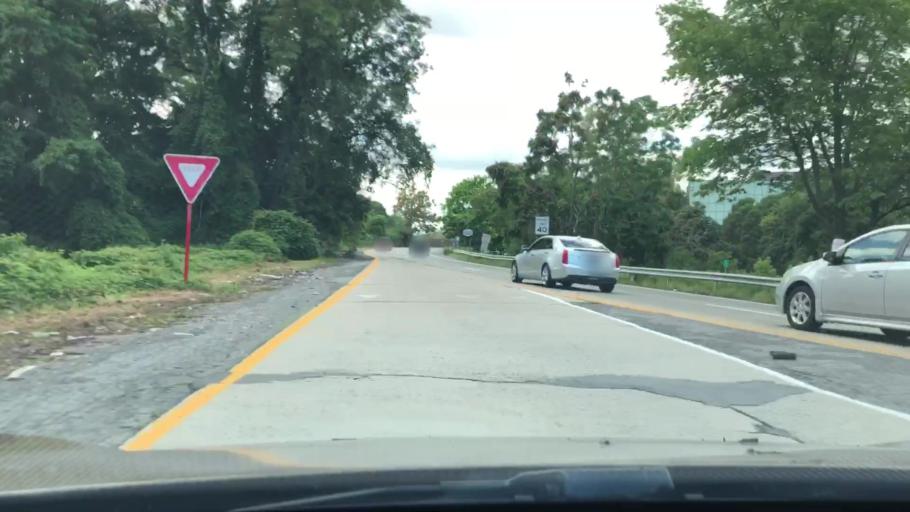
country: US
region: New York
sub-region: Westchester County
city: Rye Brook
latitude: 41.0088
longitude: -73.6968
